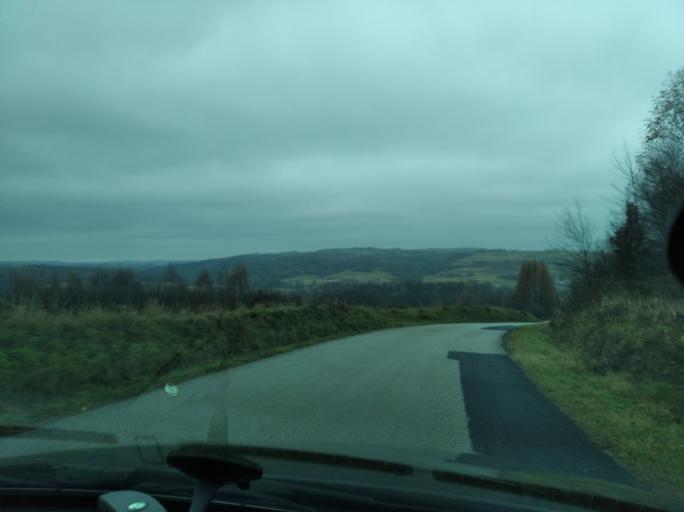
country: PL
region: Subcarpathian Voivodeship
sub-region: Powiat przeworski
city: Jawornik Polski
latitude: 49.9054
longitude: 22.2779
